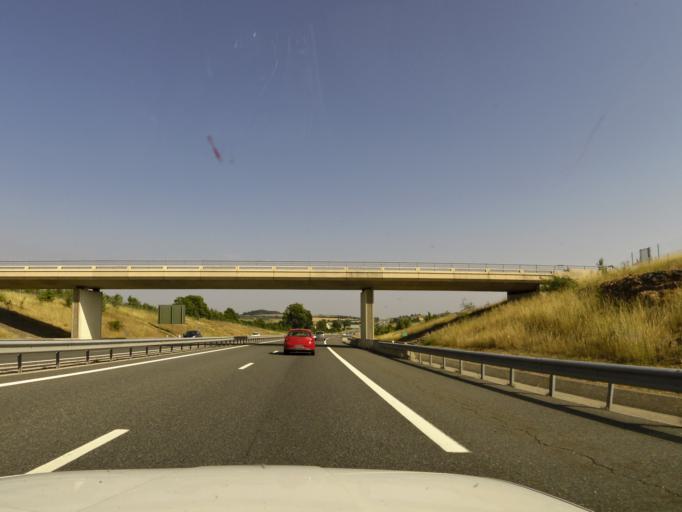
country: FR
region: Midi-Pyrenees
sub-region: Departement de l'Aveyron
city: La Cavalerie
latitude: 43.9955
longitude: 3.1712
